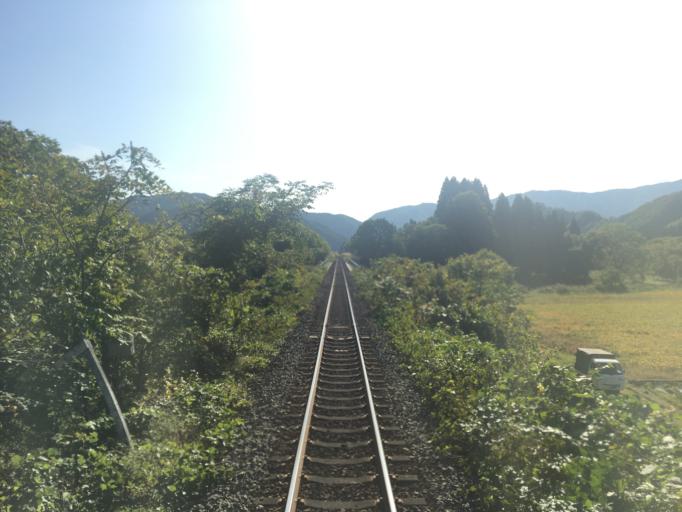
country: JP
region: Akita
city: Kakunodatemachi
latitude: 39.7469
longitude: 140.5937
